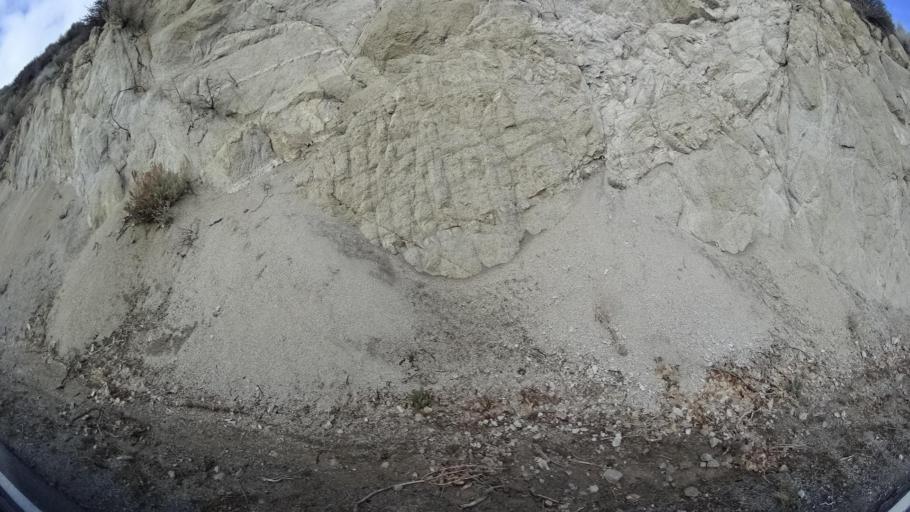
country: US
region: Nevada
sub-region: Washoe County
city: Cold Springs
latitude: 39.8328
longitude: -119.9374
